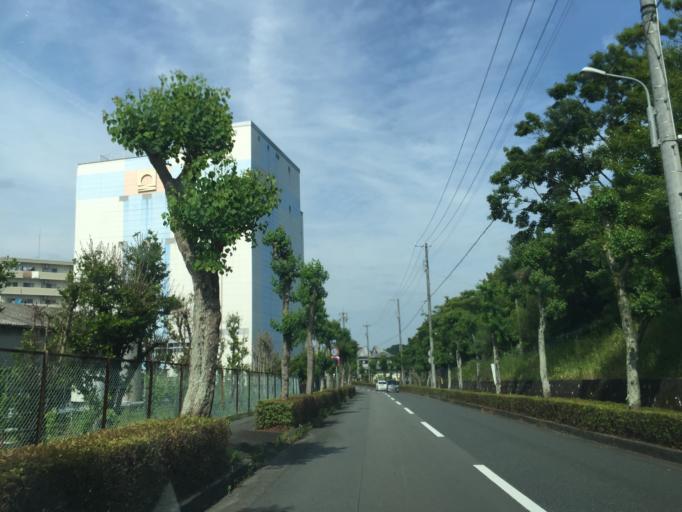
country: JP
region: Shizuoka
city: Kakegawa
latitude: 34.7632
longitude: 138.0105
